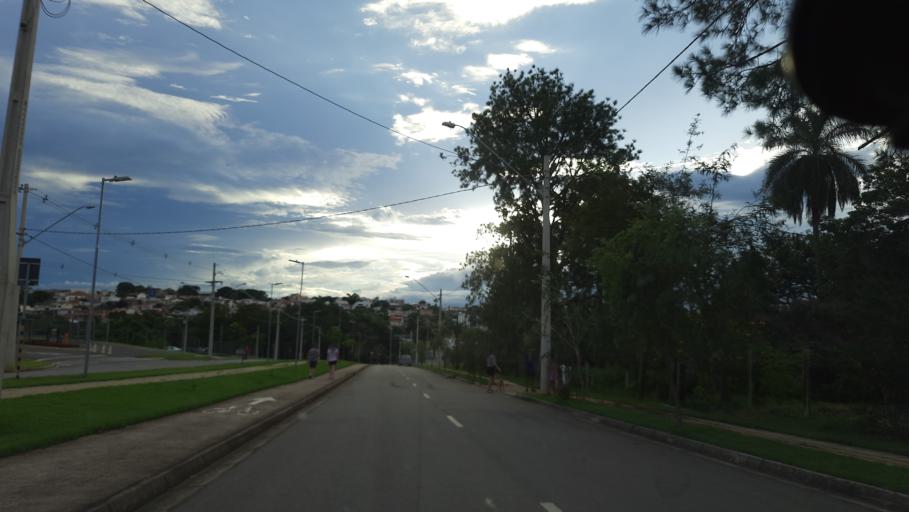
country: BR
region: Sao Paulo
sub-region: Sao Joao Da Boa Vista
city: Sao Joao da Boa Vista
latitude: -21.9626
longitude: -46.7839
